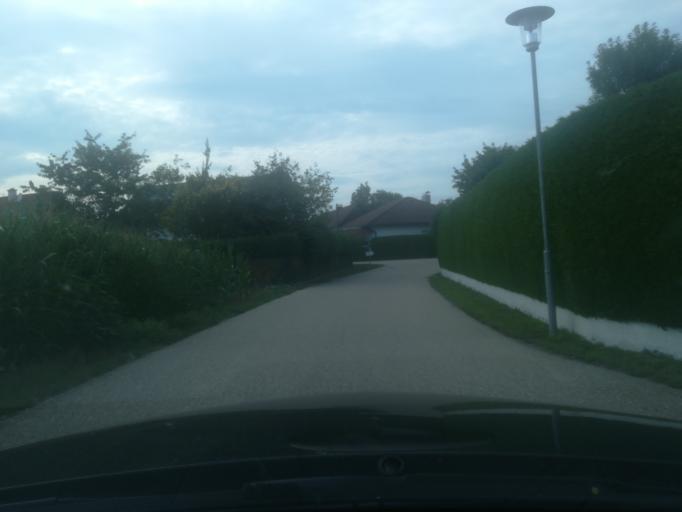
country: AT
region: Upper Austria
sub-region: Wels-Land
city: Marchtrenk
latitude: 48.1860
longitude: 14.1317
